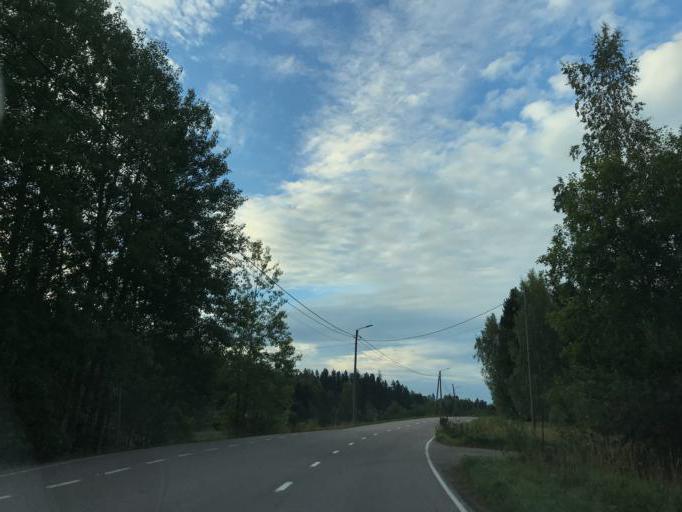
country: FI
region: Uusimaa
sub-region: Helsinki
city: Vihti
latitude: 60.3968
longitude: 24.5094
